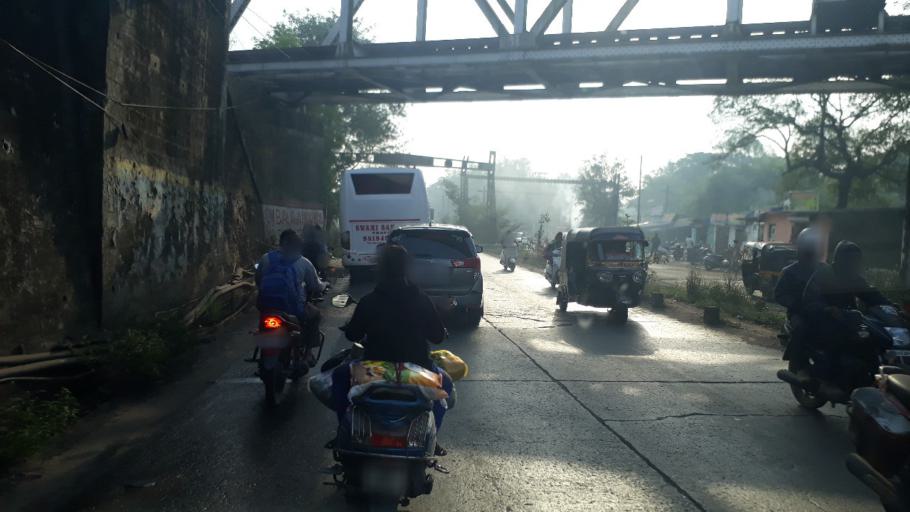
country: IN
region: Maharashtra
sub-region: Raigarh
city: Kalundri
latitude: 18.9750
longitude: 73.1236
